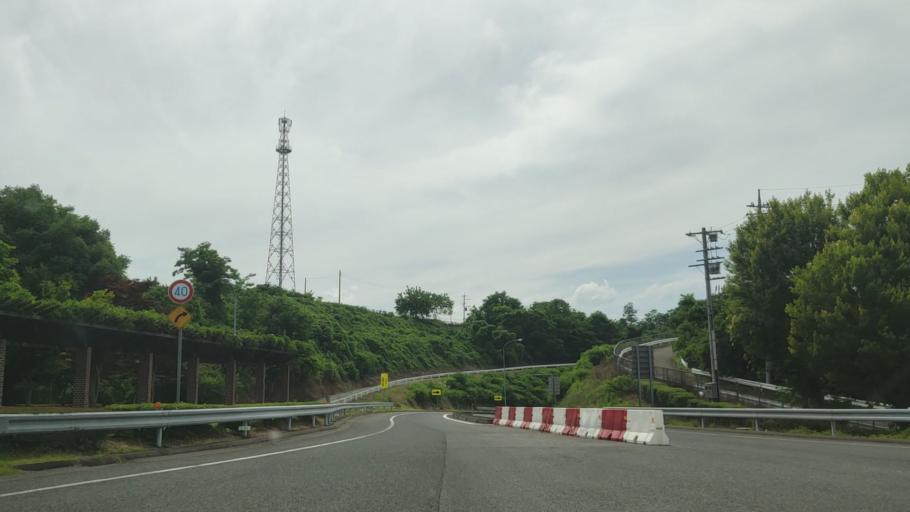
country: JP
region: Gunma
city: Tomioka
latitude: 36.2407
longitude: 138.8919
